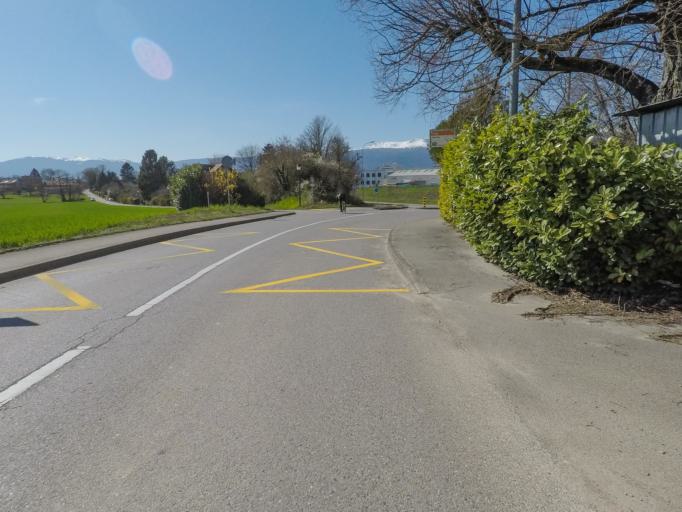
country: CH
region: Geneva
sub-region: Geneva
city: Vernier
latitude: 46.2166
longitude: 6.0689
